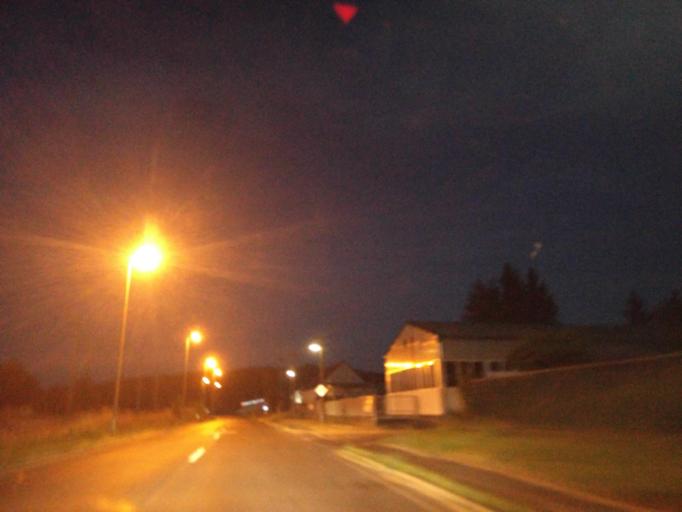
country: HU
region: Vas
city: Vasvar
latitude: 47.0574
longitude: 16.8106
